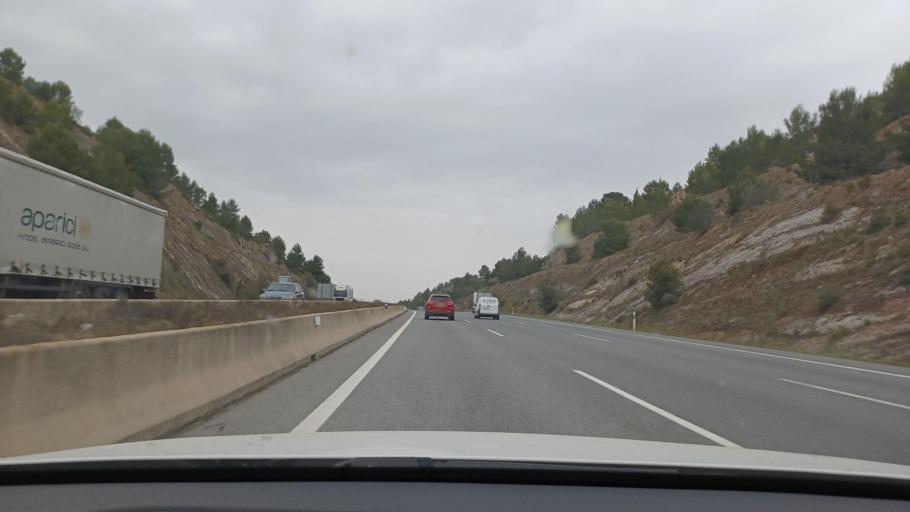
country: ES
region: Valencia
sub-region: Provincia de Valencia
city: Llosa de Ranes
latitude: 39.0302
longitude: -0.5513
